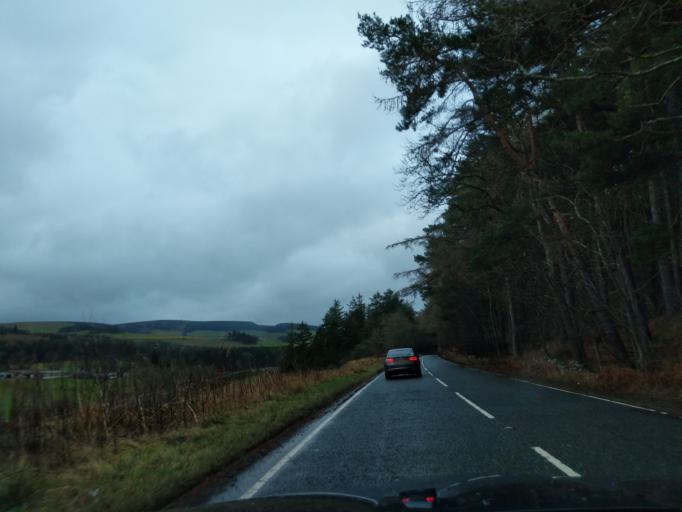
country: GB
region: Scotland
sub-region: The Scottish Borders
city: Galashiels
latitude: 55.6479
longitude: -2.8585
